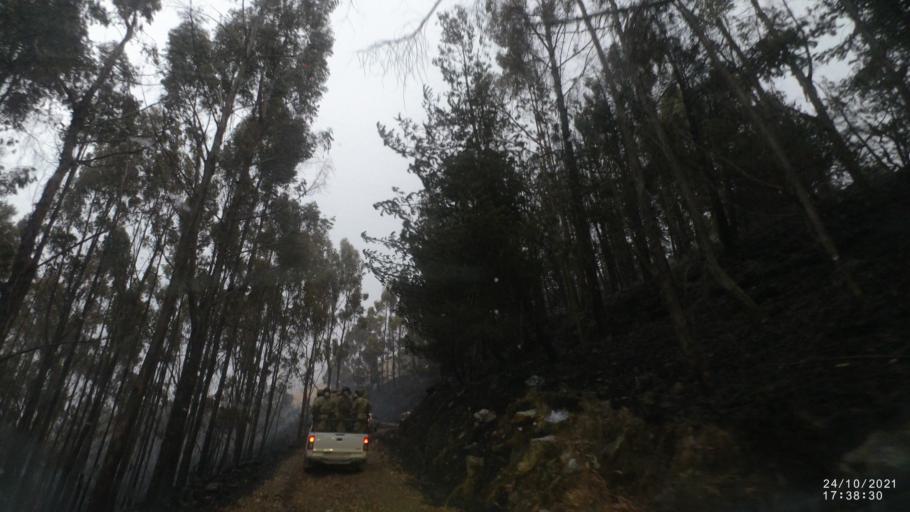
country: BO
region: Cochabamba
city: Cochabamba
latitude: -17.3171
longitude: -66.1307
